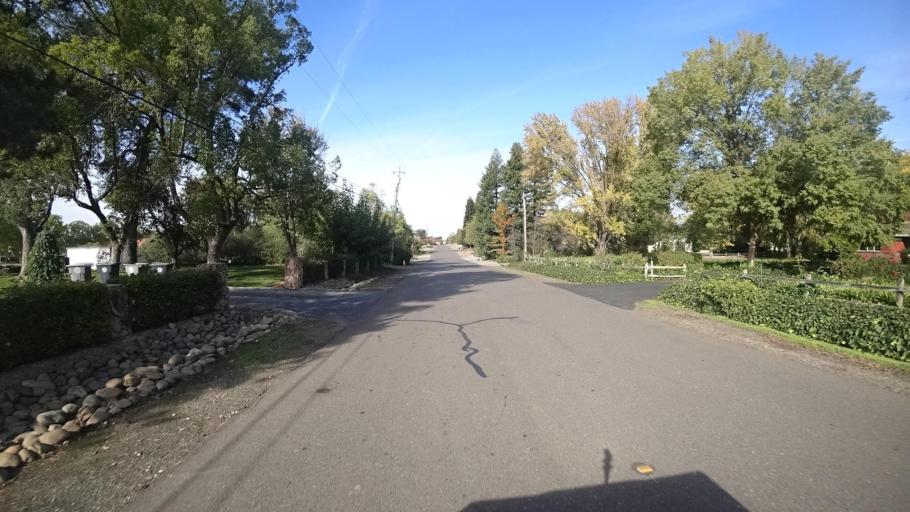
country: US
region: California
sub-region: Sacramento County
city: Vineyard
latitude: 38.4409
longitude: -121.3610
